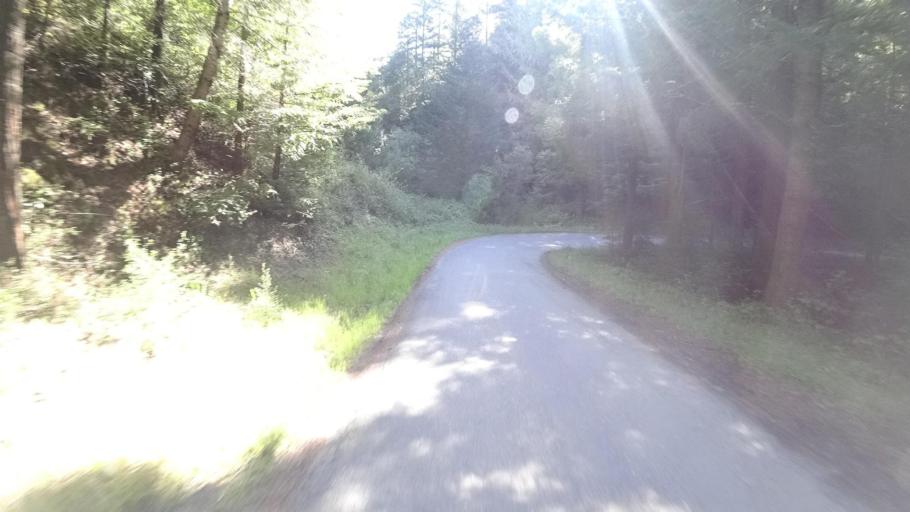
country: US
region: California
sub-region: Humboldt County
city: Rio Dell
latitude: 40.4604
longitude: -123.9951
